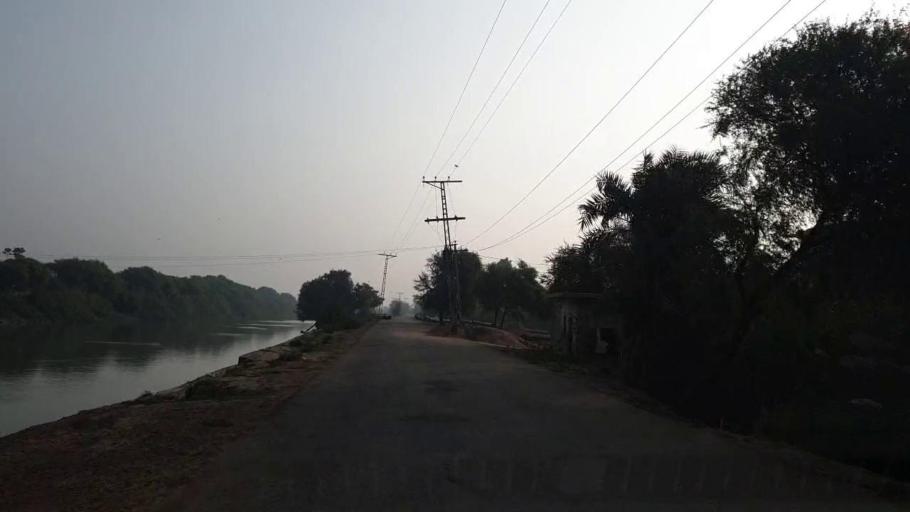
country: PK
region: Sindh
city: Tando Muhammad Khan
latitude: 25.1264
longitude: 68.5495
